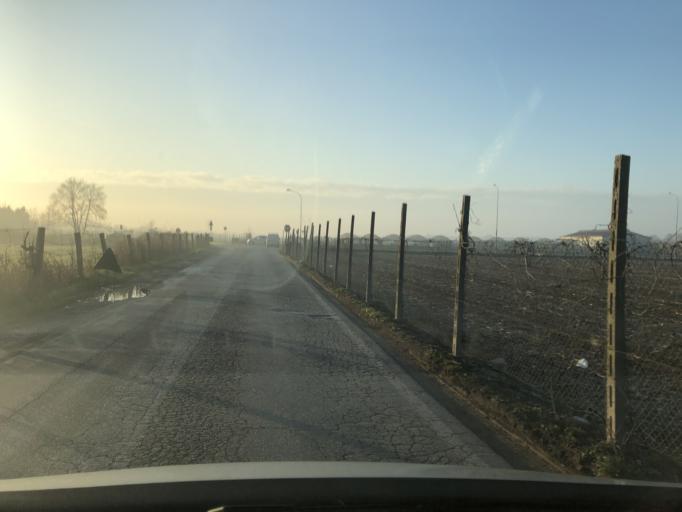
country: IT
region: Veneto
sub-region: Provincia di Verona
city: Caselle
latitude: 45.4098
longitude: 10.8772
